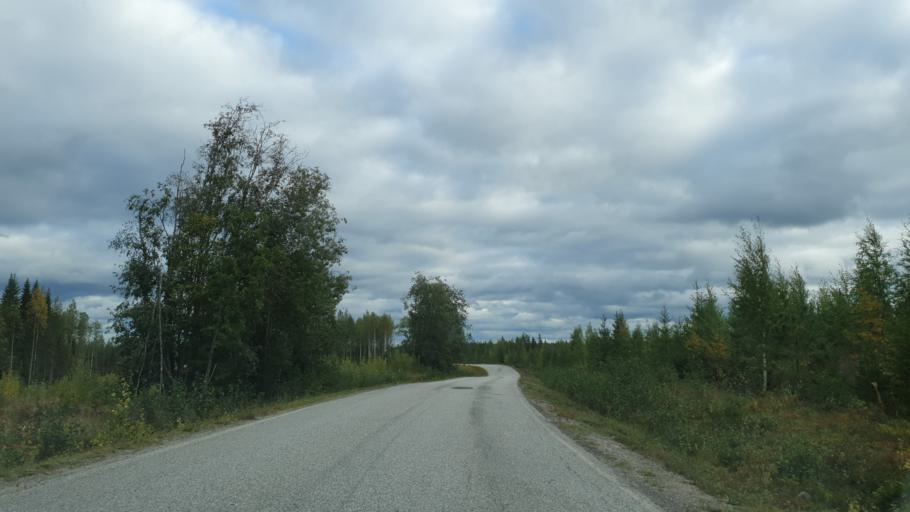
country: FI
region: Kainuu
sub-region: Kehys-Kainuu
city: Kuhmo
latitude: 63.9526
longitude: 29.7452
